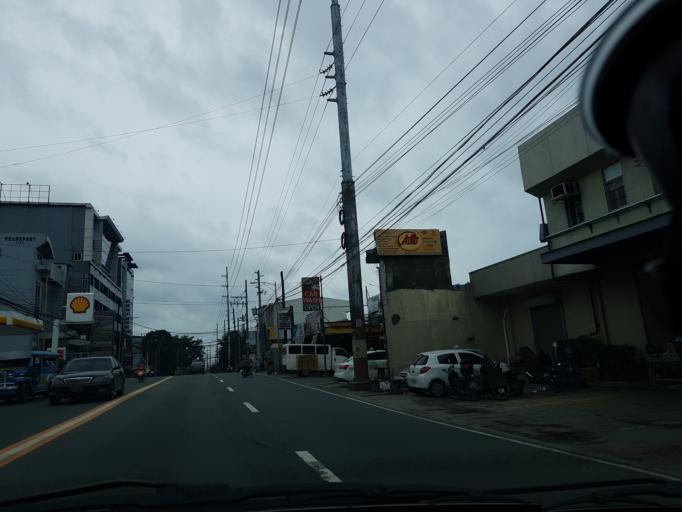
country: PH
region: Metro Manila
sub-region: Pasig
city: Pasig City
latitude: 14.5665
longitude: 121.0659
